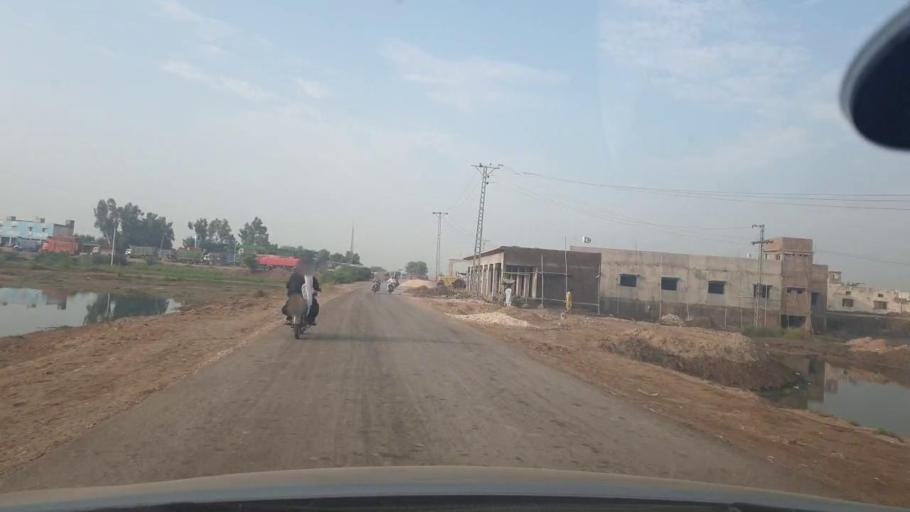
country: PK
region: Sindh
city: Jacobabad
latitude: 28.2642
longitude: 68.4177
